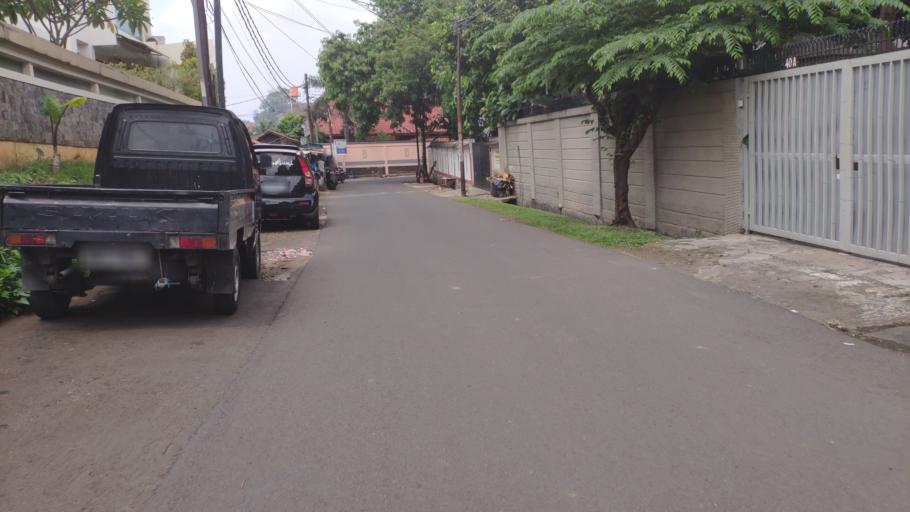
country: ID
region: Jakarta Raya
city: Jakarta
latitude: -6.2698
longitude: 106.8260
